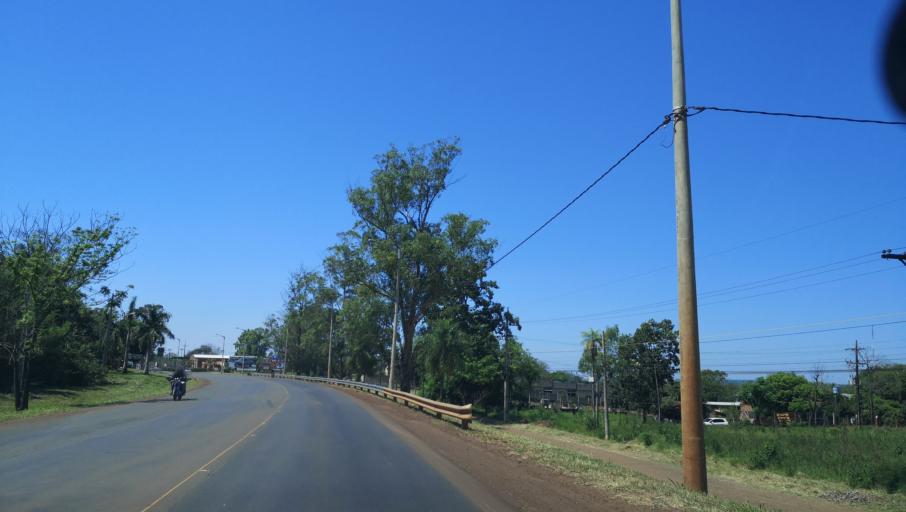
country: PY
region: Itapua
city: San Juan del Parana
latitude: -27.2916
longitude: -55.9343
